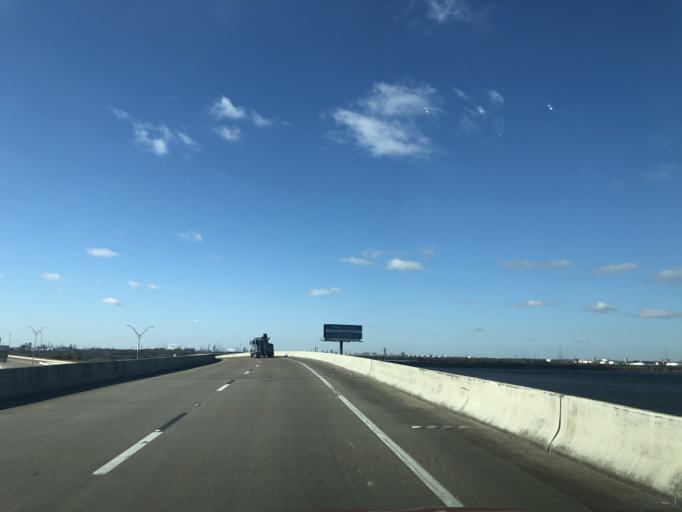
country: US
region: Texas
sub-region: Harris County
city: Baytown
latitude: 29.7141
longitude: -94.9999
